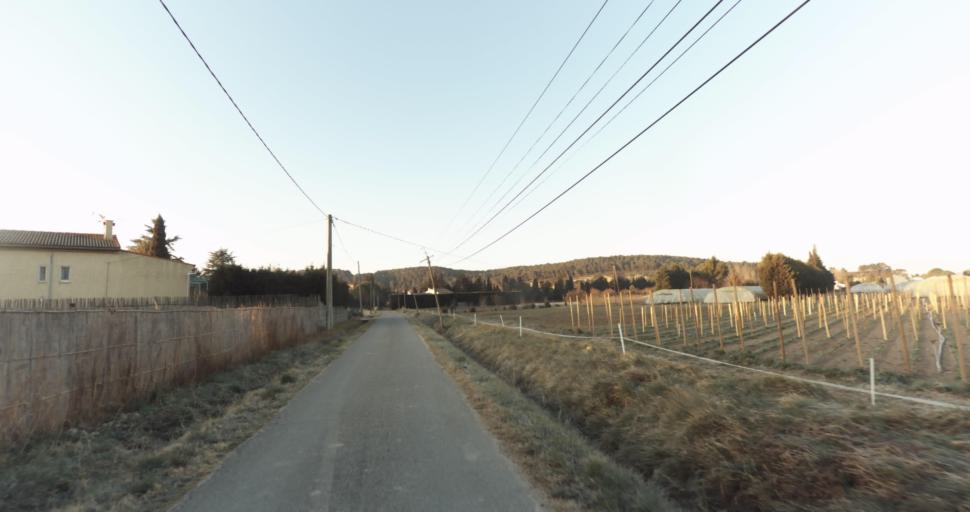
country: FR
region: Provence-Alpes-Cote d'Azur
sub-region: Departement des Bouches-du-Rhone
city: Barbentane
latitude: 43.9021
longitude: 4.7704
